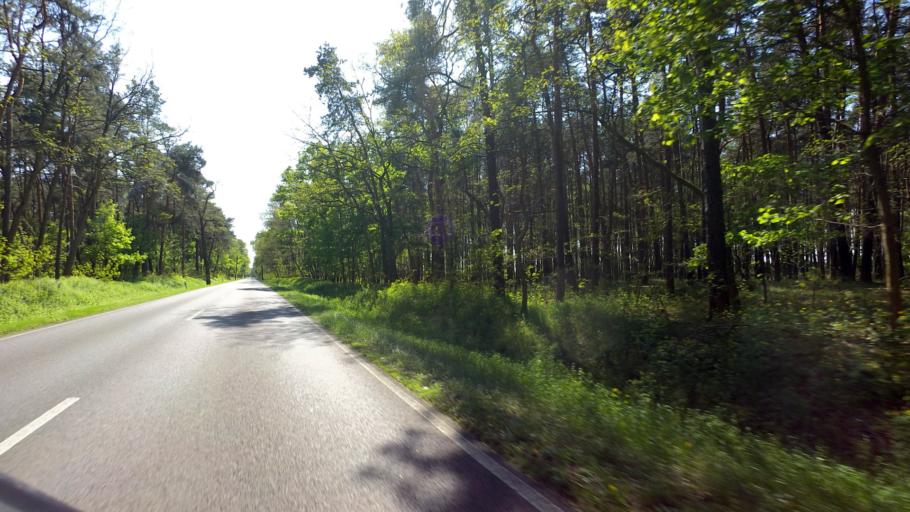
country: DE
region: Brandenburg
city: Tauche
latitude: 52.1269
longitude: 14.1968
